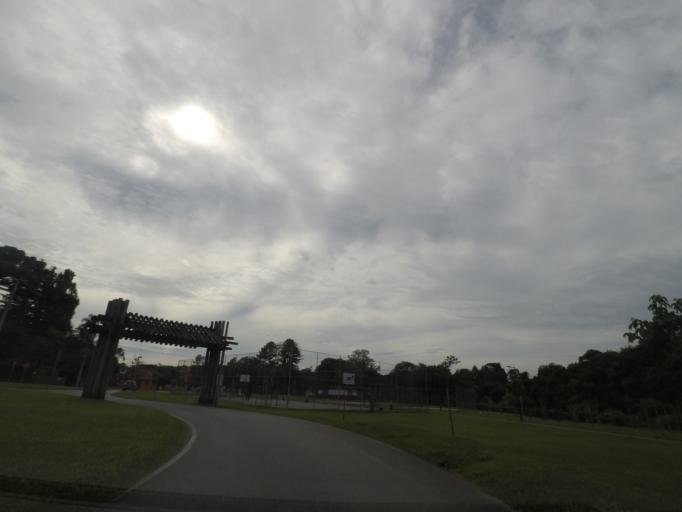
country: BR
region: Parana
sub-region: Curitiba
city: Curitiba
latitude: -25.3878
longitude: -49.3047
